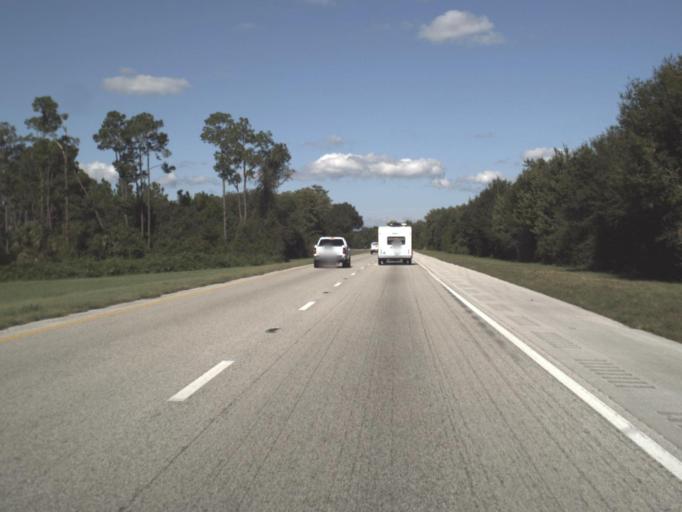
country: US
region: Florida
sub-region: Osceola County
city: Saint Cloud
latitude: 28.0515
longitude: -81.2197
